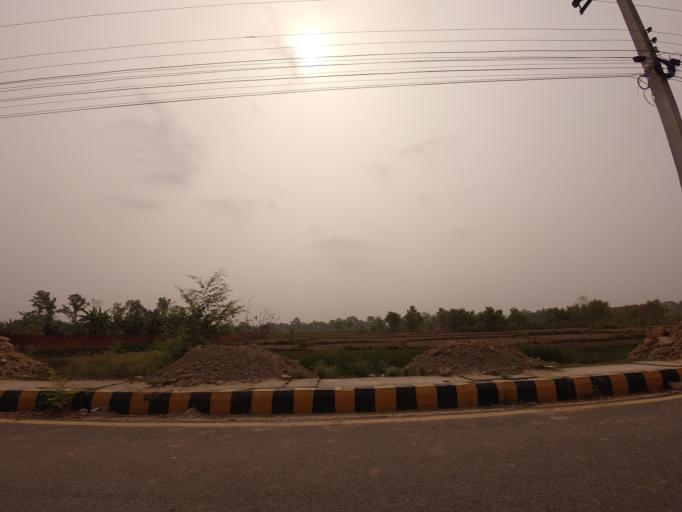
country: IN
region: Uttar Pradesh
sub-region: Maharajganj
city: Nautanwa
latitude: 27.4818
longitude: 83.2842
